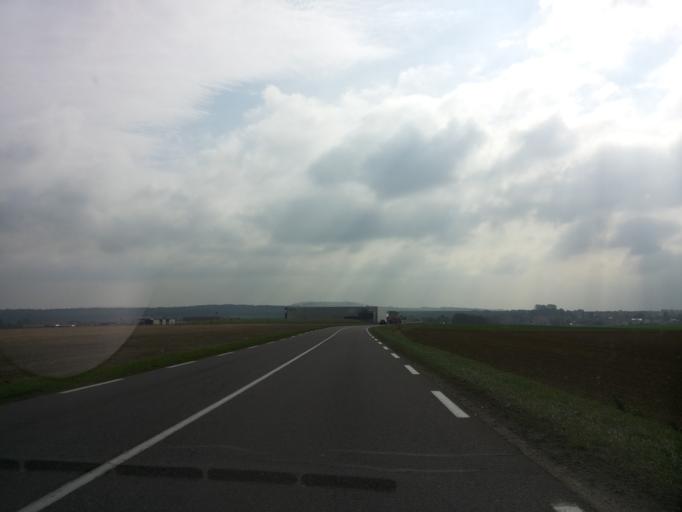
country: FR
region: Lorraine
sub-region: Departement de la Moselle
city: Solgne
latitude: 48.9779
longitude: 6.2911
